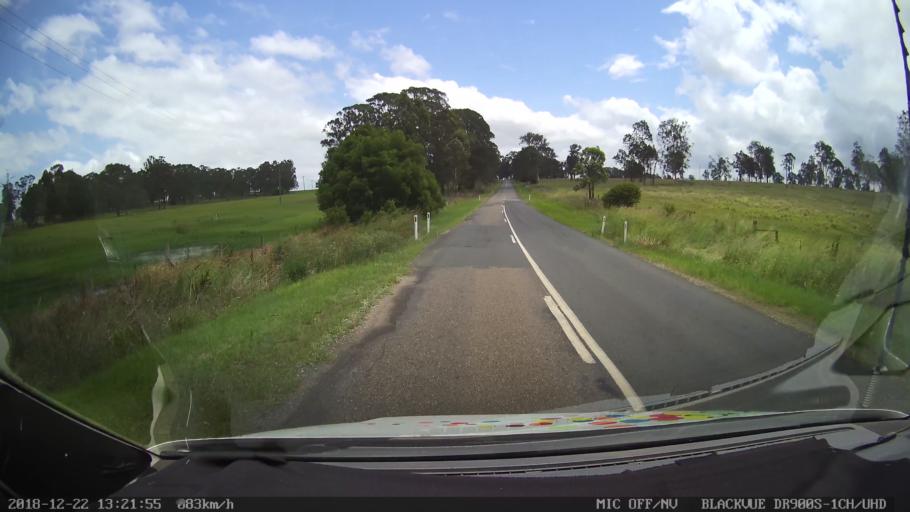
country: AU
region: New South Wales
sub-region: Clarence Valley
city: Coutts Crossing
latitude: -29.7817
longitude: 152.9160
